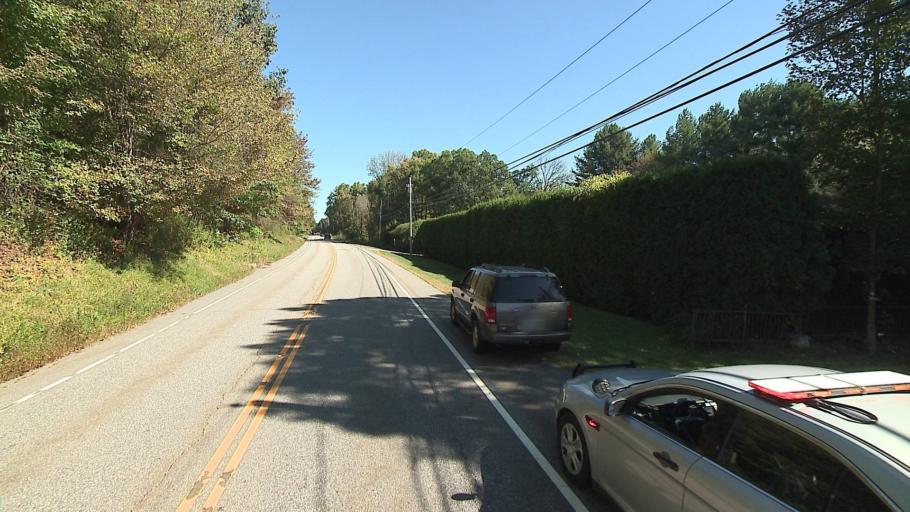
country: US
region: Connecticut
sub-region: Litchfield County
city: New Preston
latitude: 41.7044
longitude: -73.2760
